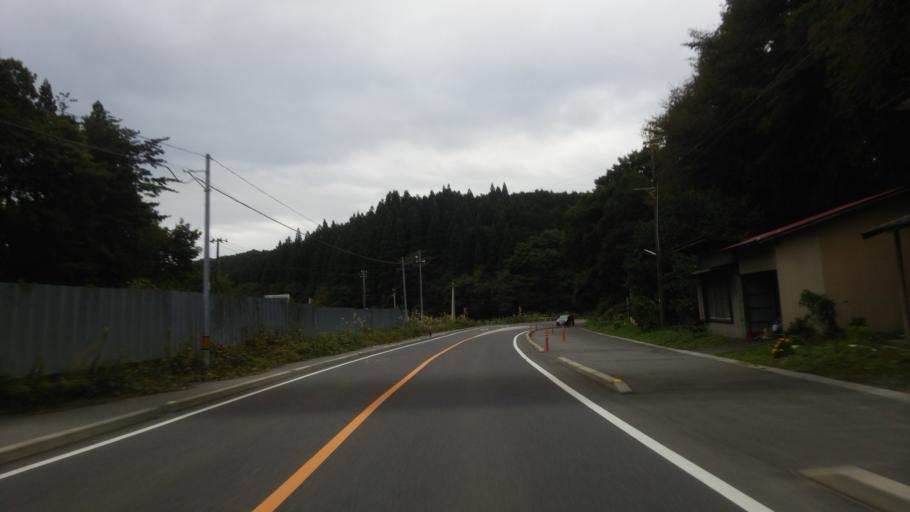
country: JP
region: Fukushima
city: Sukagawa
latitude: 37.1684
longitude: 140.2210
